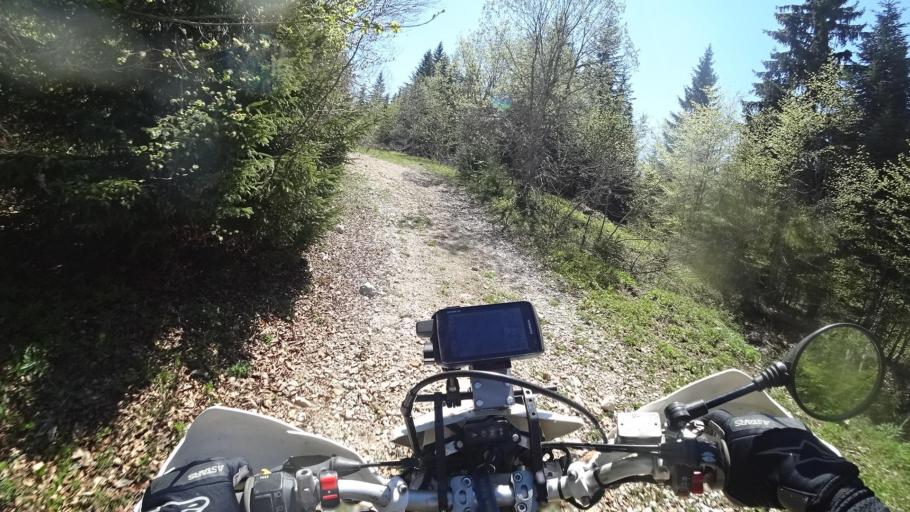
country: BA
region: Federation of Bosnia and Herzegovina
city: Rumboci
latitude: 43.8677
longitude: 17.4883
